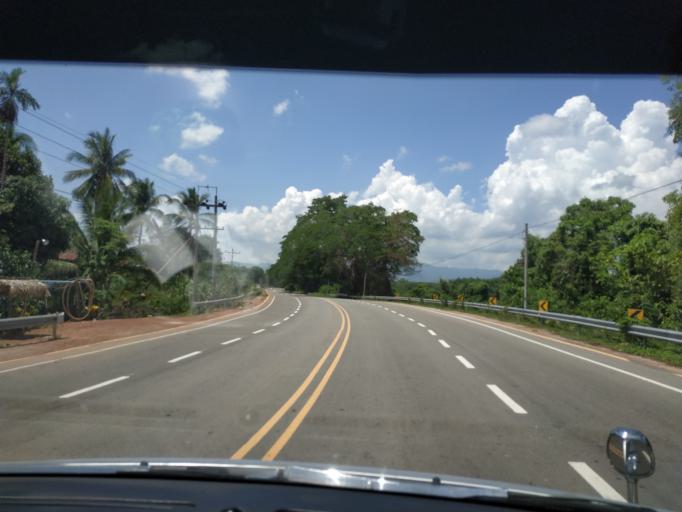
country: MM
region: Mon
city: Kyaikto
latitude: 17.3468
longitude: 97.0379
